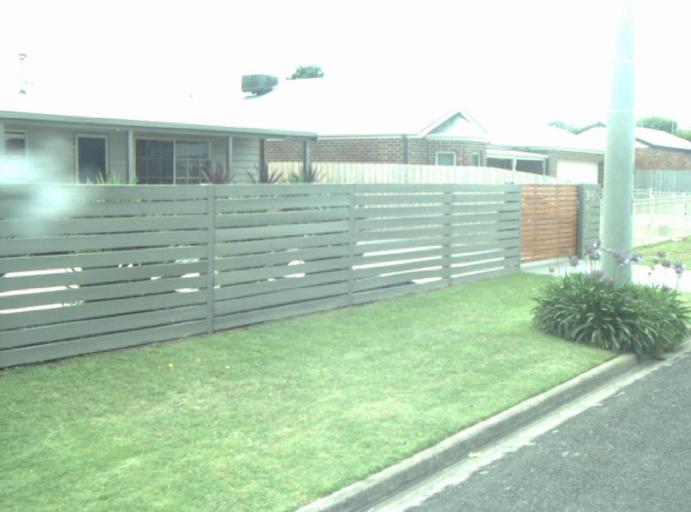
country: AU
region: Victoria
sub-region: Greater Geelong
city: Clifton Springs
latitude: -38.2656
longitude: 144.5526
